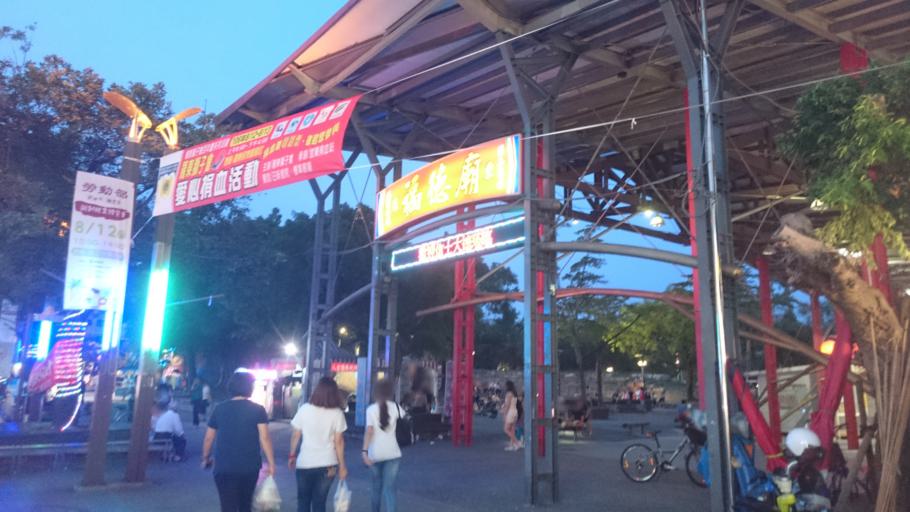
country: TW
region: Taiwan
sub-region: Yilan
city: Yilan
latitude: 24.6760
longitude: 121.7679
